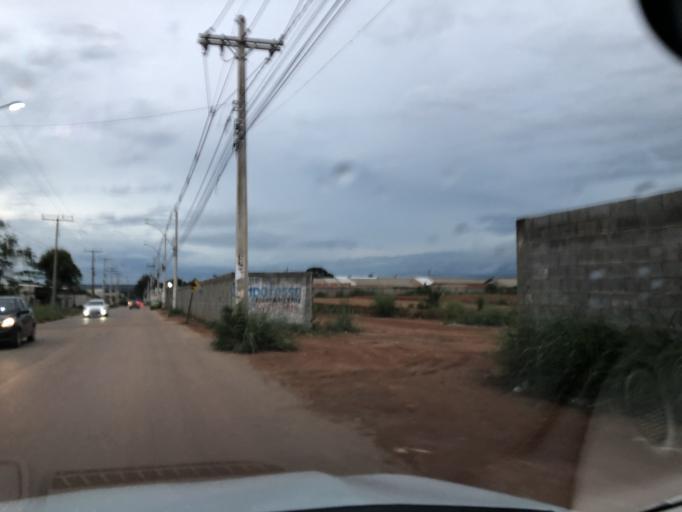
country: BR
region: Goias
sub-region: Luziania
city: Luziania
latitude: -16.1091
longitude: -47.9822
